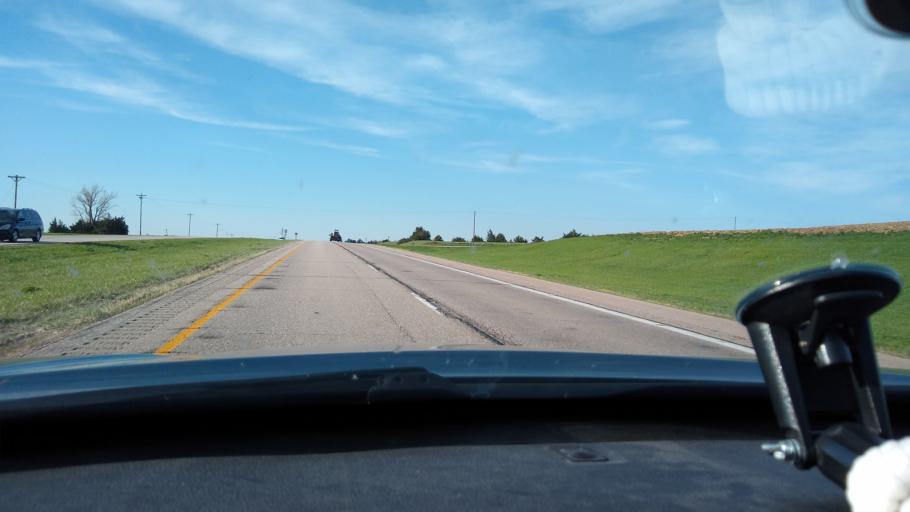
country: US
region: Nebraska
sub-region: York County
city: York
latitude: 40.7835
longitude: -97.5977
